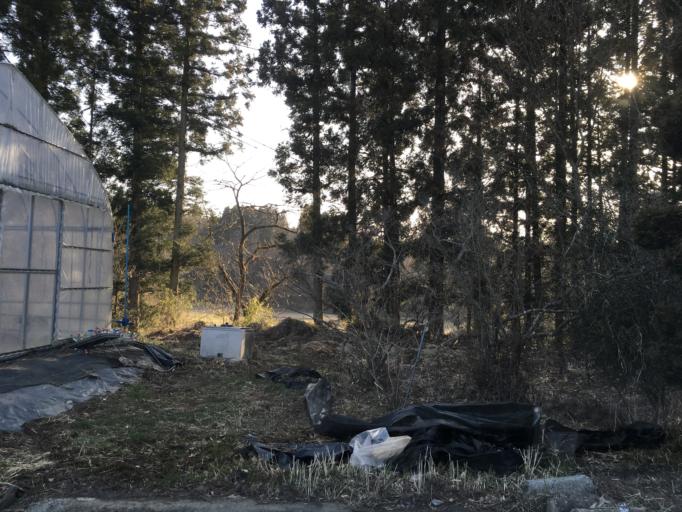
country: JP
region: Iwate
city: Ichinoseki
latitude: 38.8362
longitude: 141.1356
